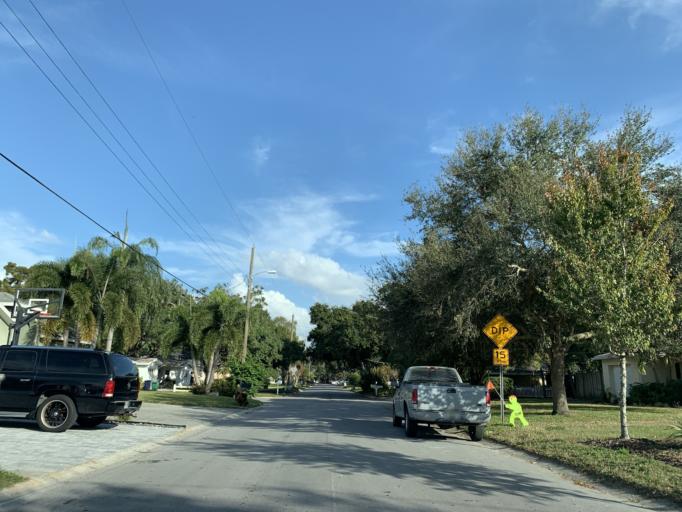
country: US
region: Florida
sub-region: Hillsborough County
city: Tampa
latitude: 27.8977
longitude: -82.5005
